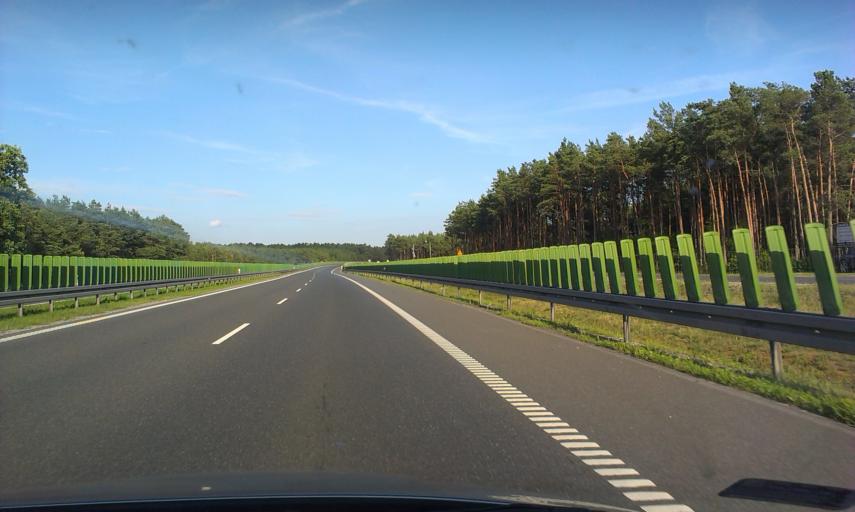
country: PL
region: Kujawsko-Pomorskie
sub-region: Powiat bydgoski
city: Biale Blota
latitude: 53.0561
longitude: 17.9729
